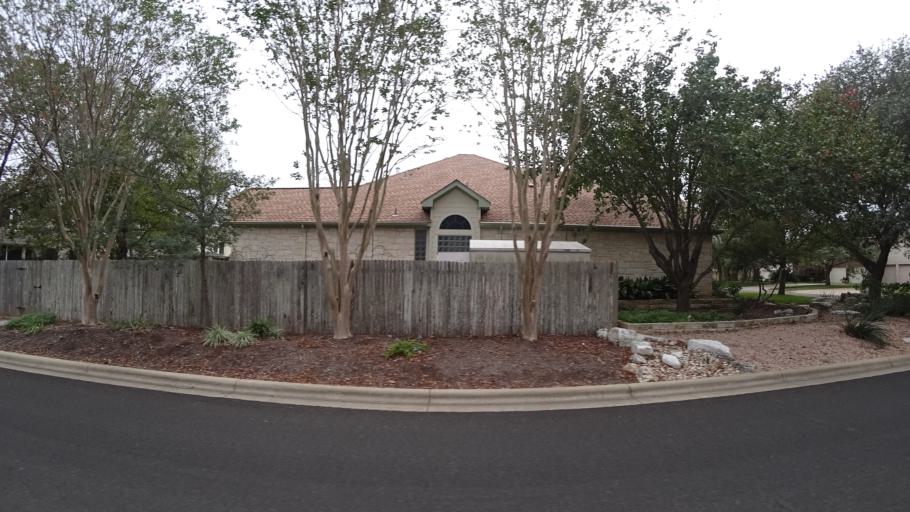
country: US
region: Texas
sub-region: Travis County
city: Shady Hollow
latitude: 30.1857
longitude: -97.8873
